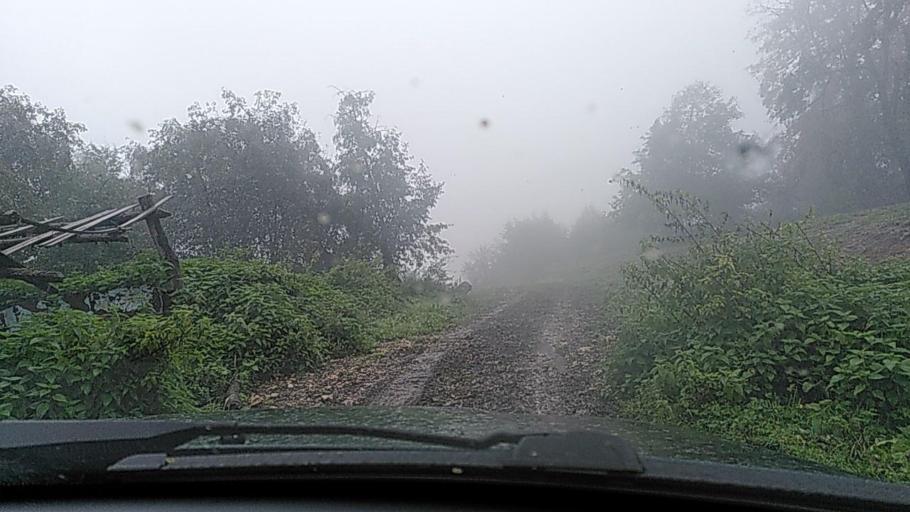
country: RU
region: Kabardino-Balkariya
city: Belaya Rechka
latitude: 43.3560
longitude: 43.3996
